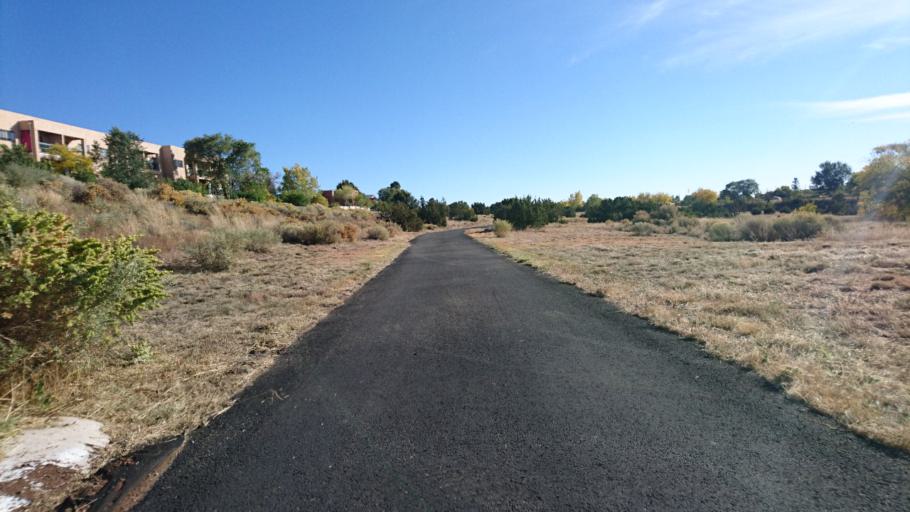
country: US
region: New Mexico
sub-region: Santa Fe County
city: Santa Fe
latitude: 35.6578
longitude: -105.9648
